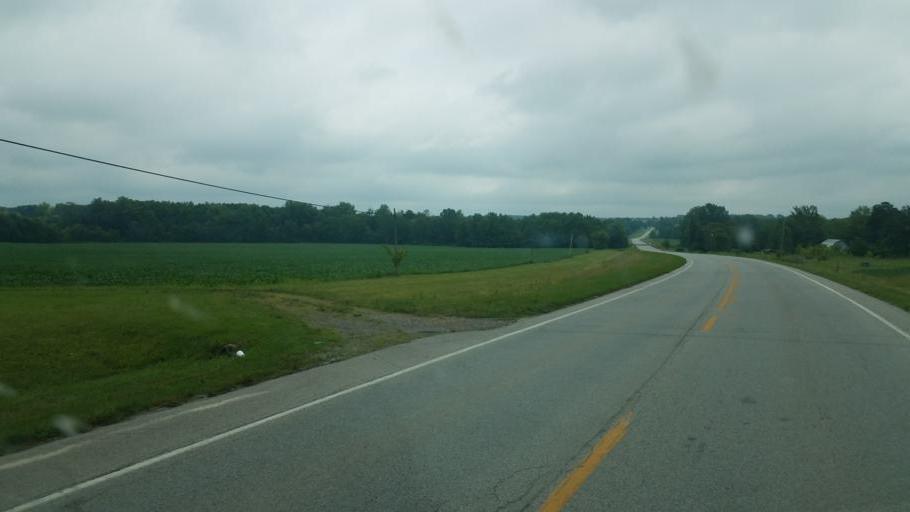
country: US
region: Ohio
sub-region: Highland County
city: Hillsboro
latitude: 39.2109
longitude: -83.5555
